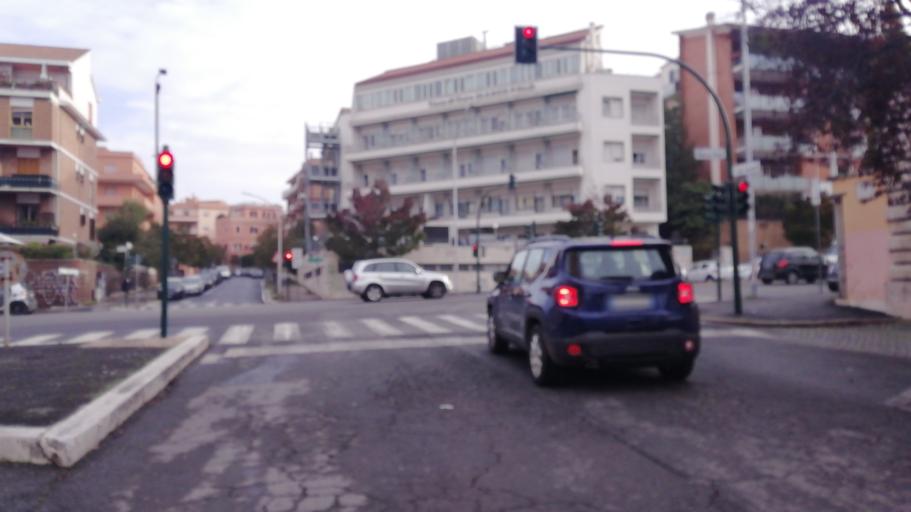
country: IT
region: Latium
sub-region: Citta metropolitana di Roma Capitale
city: Rome
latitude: 41.8744
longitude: 12.4857
